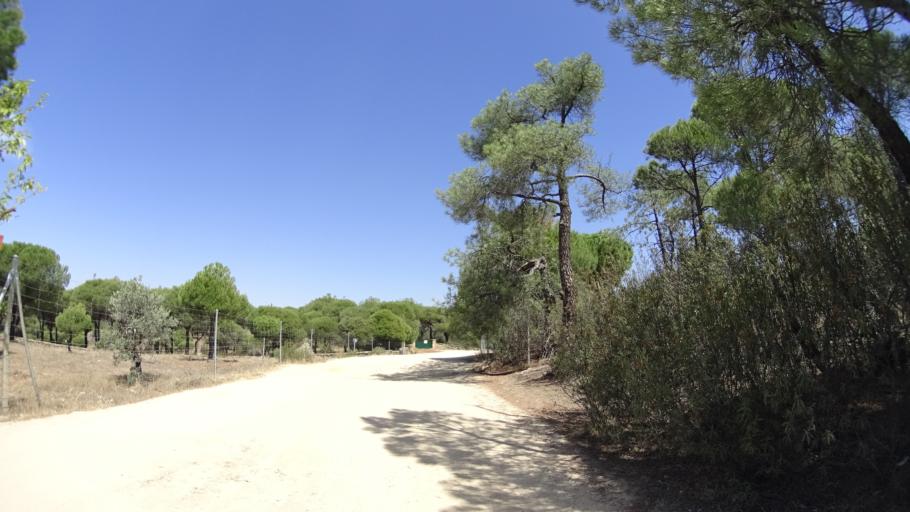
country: ES
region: Madrid
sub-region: Provincia de Madrid
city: Torrelodones
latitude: 40.5642
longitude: -3.9389
